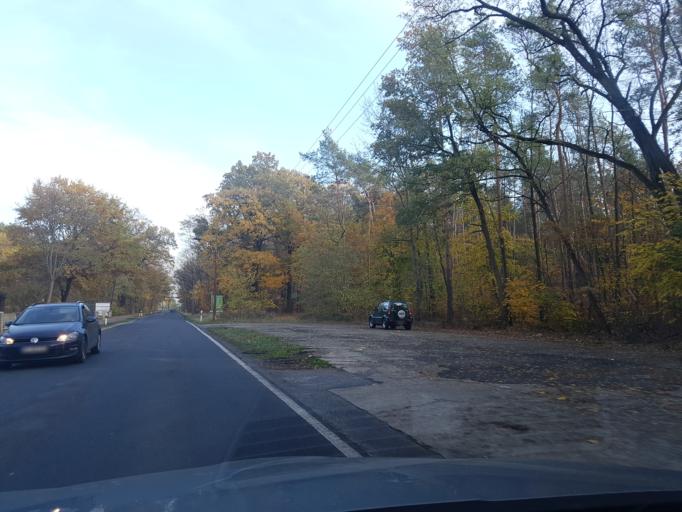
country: DE
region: Brandenburg
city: Falkenberg
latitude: 51.5879
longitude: 13.2701
